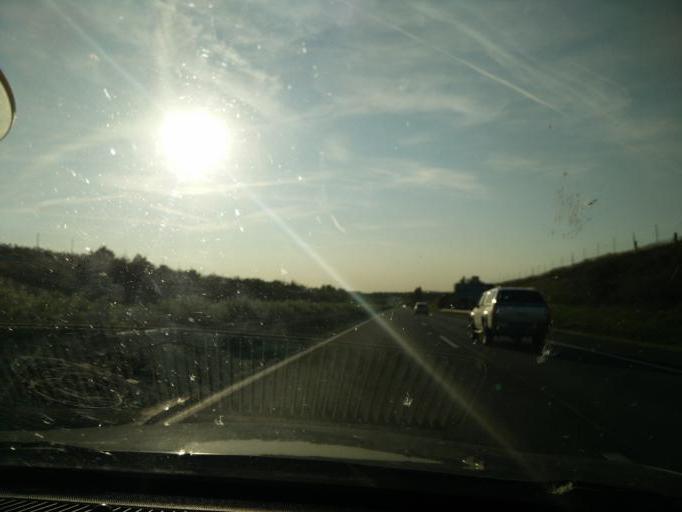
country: HU
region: Pest
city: Biatorbagy
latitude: 47.5033
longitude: 18.7763
